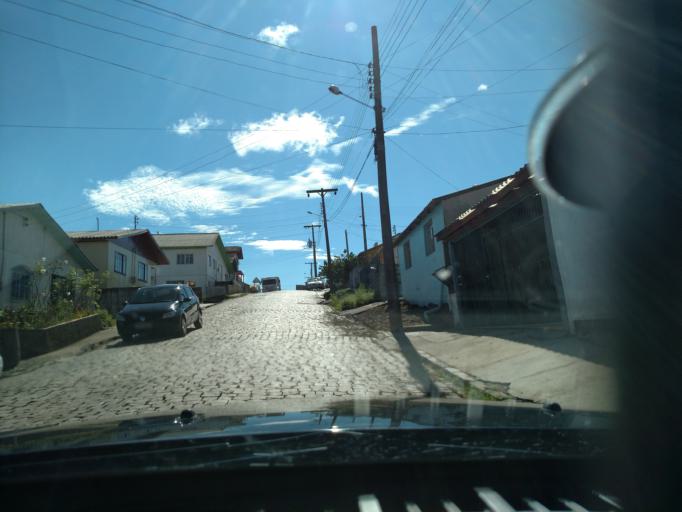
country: BR
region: Santa Catarina
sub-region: Sao Joaquim
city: Sao Joaquim
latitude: -28.2915
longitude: -49.9288
